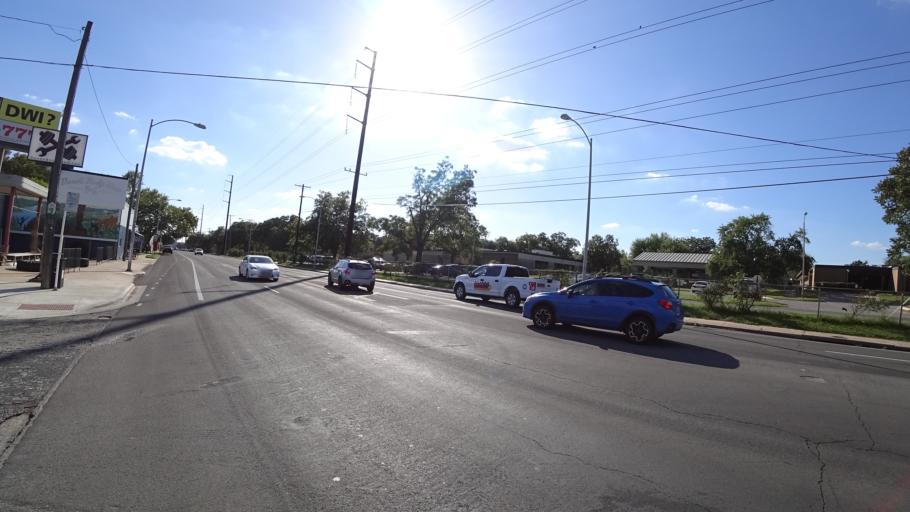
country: US
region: Texas
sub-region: Travis County
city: Austin
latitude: 30.3086
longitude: -97.7343
